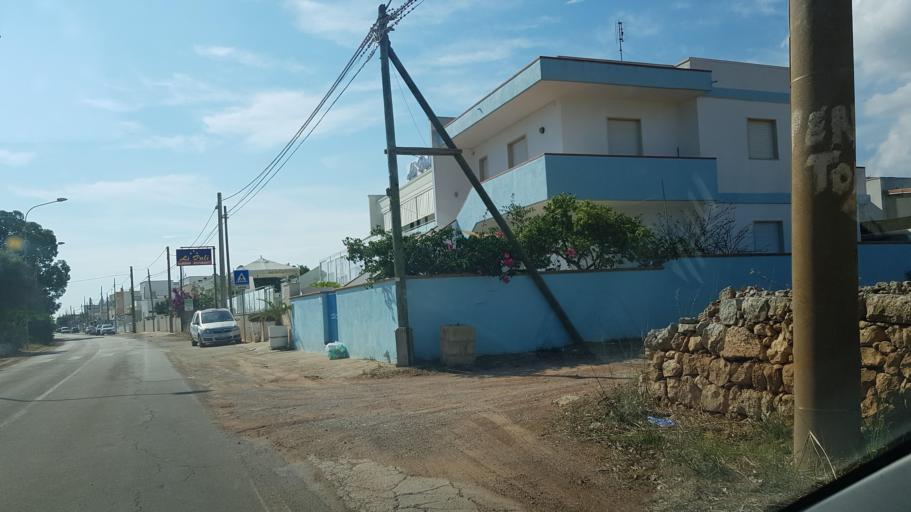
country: IT
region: Apulia
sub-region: Provincia di Lecce
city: Gemini
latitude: 39.8437
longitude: 18.2131
